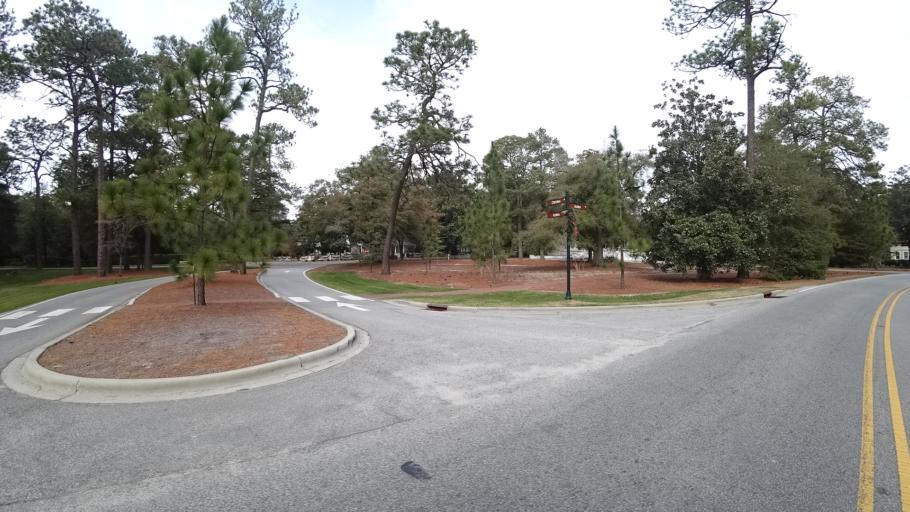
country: US
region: North Carolina
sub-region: Moore County
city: Pinehurst
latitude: 35.1930
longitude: -79.4703
